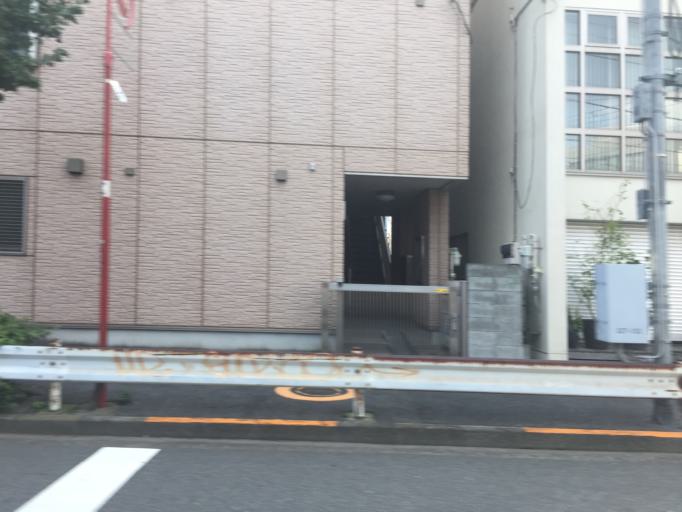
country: JP
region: Tokyo
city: Tokyo
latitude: 35.6241
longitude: 139.6550
